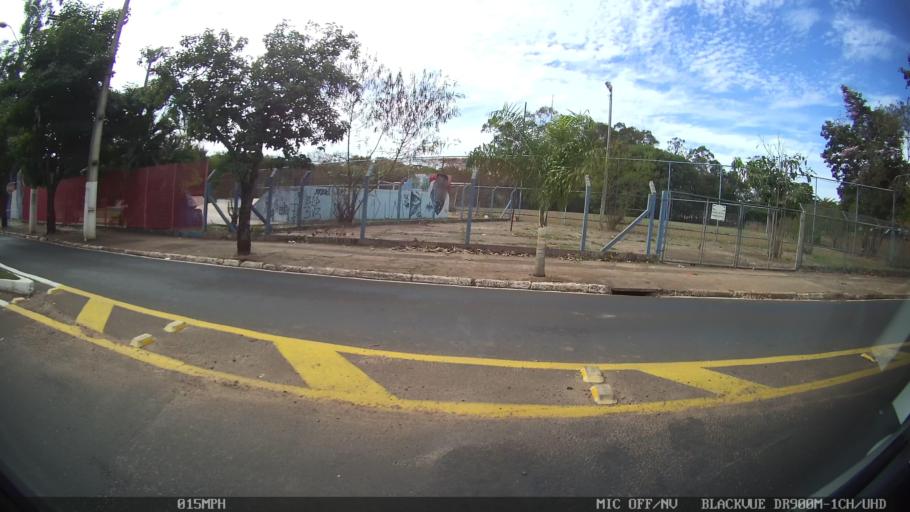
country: BR
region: Sao Paulo
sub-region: Catanduva
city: Catanduva
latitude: -21.1395
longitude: -48.9656
